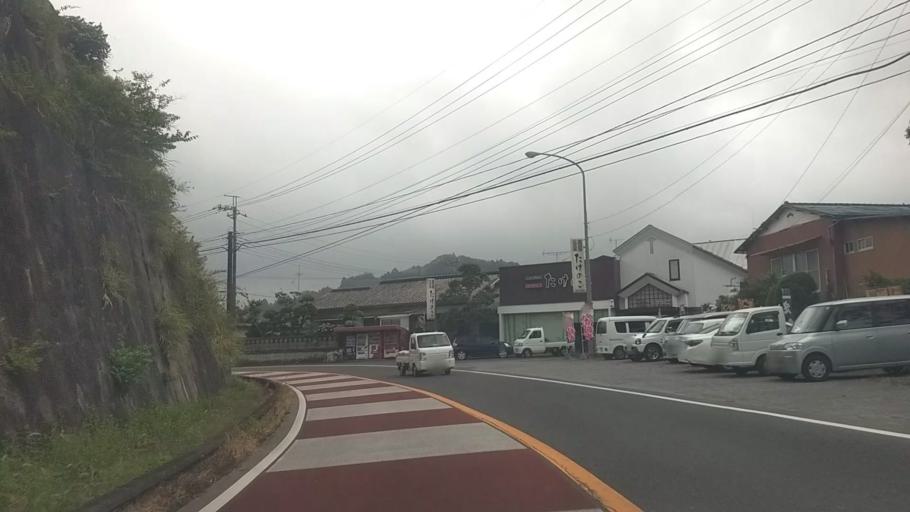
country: JP
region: Chiba
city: Katsuura
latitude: 35.2416
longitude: 140.2381
